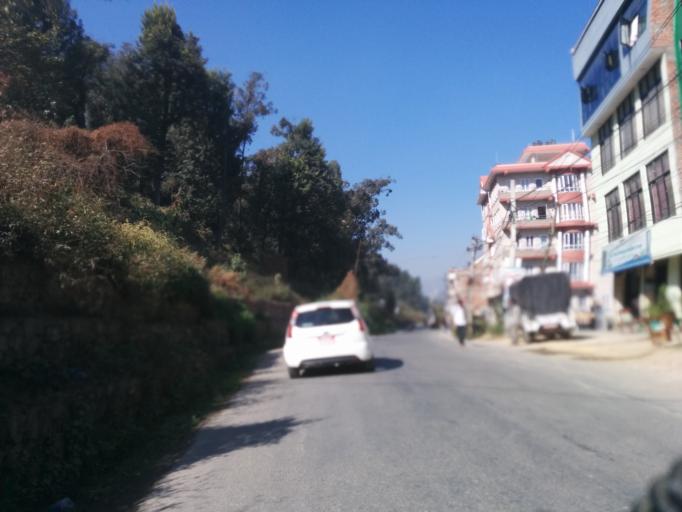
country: NP
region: Central Region
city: Kirtipur
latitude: 27.6786
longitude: 85.2793
